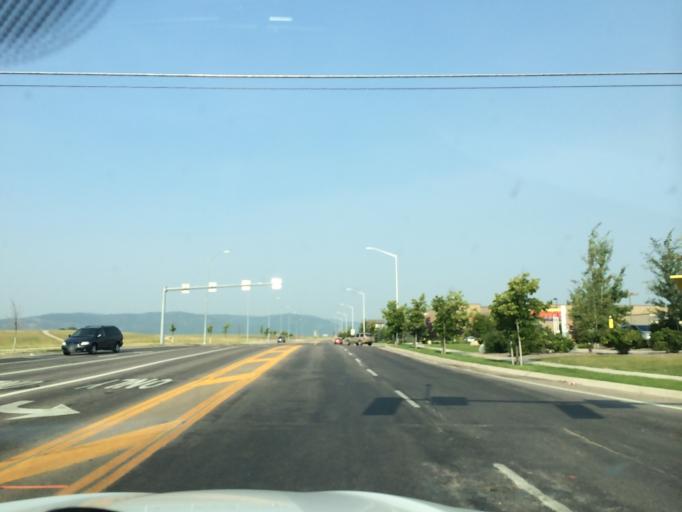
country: US
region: Montana
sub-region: Flathead County
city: Kalispell
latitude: 48.2332
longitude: -114.3308
